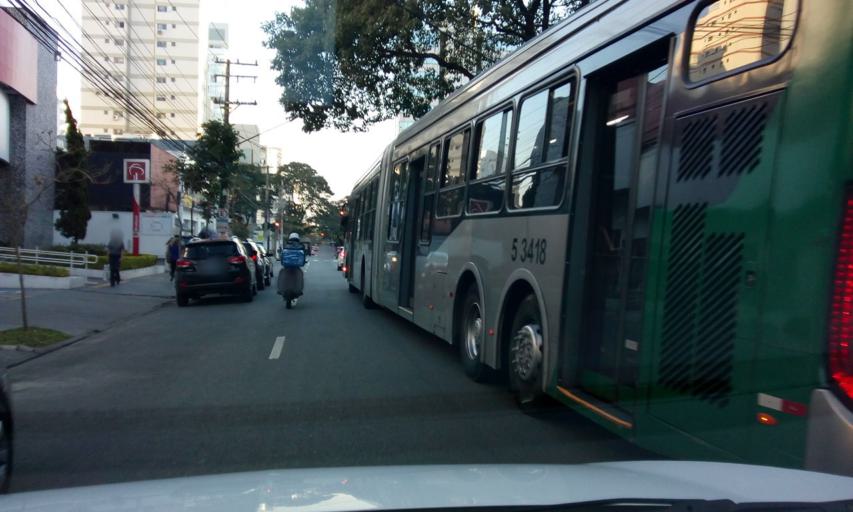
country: BR
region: Sao Paulo
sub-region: Sao Paulo
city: Sao Paulo
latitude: -23.6080
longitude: -46.6617
